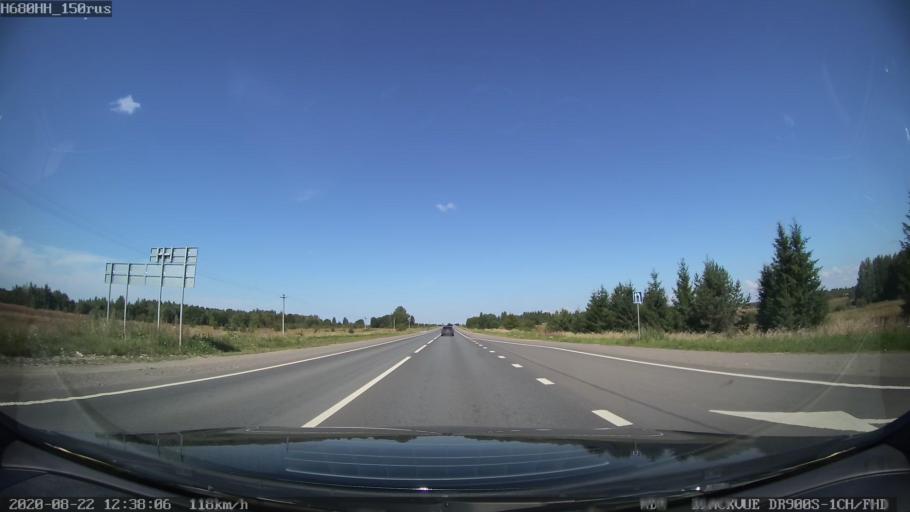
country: RU
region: Tverskaya
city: Rameshki
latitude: 57.3083
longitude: 36.0886
